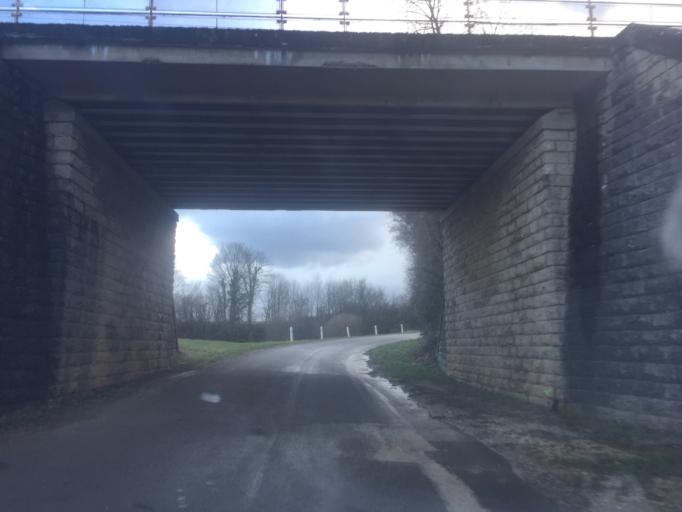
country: FR
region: Franche-Comte
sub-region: Departement du Jura
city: Fraisans
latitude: 47.1696
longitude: 5.7679
